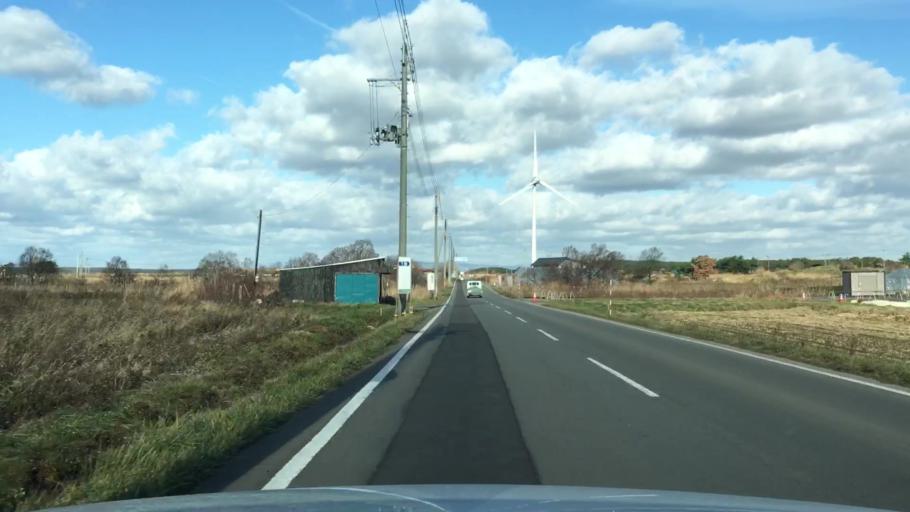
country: JP
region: Aomori
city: Shimokizukuri
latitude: 40.8574
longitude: 140.3034
